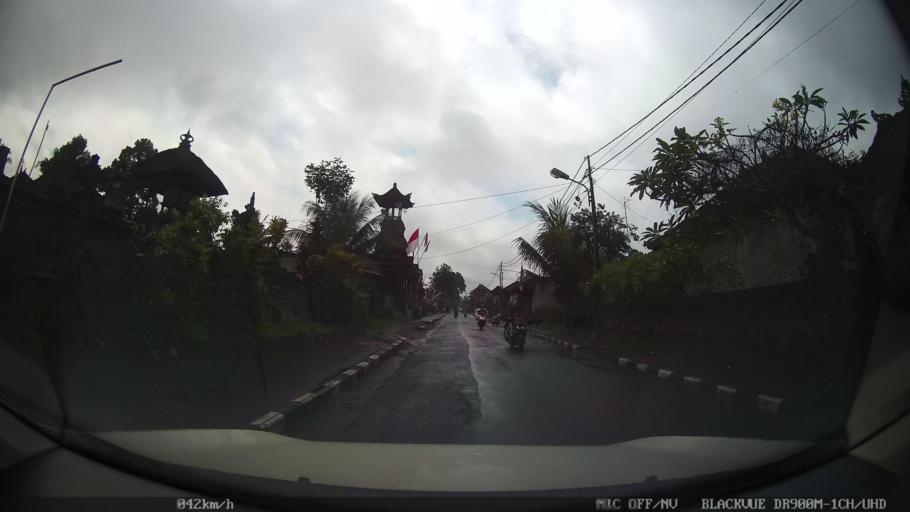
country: ID
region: Bali
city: Pegongan
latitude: -8.4915
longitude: 115.2262
